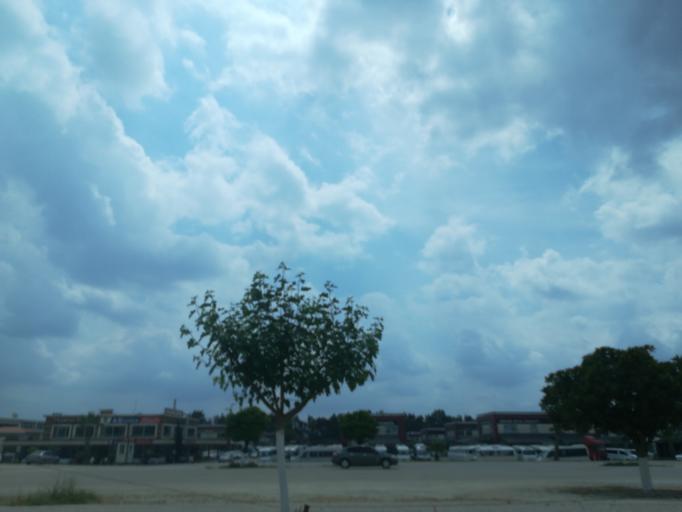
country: TR
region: Adana
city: Seyhan
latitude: 37.0010
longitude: 35.2459
